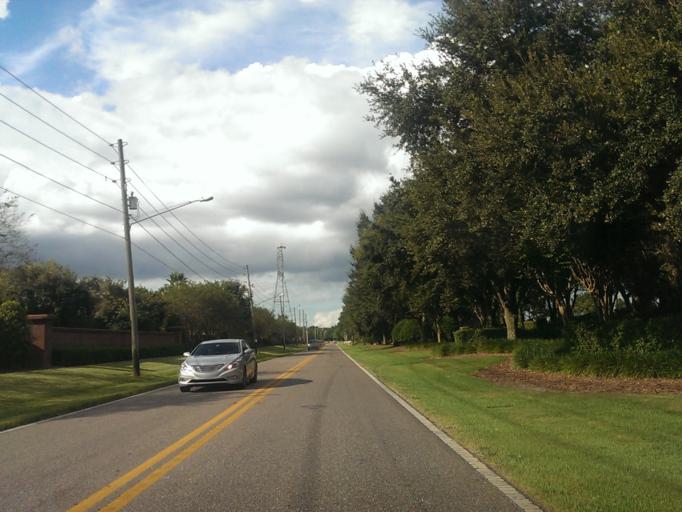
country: US
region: Florida
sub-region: Orange County
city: Bay Hill
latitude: 28.4667
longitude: -81.5412
